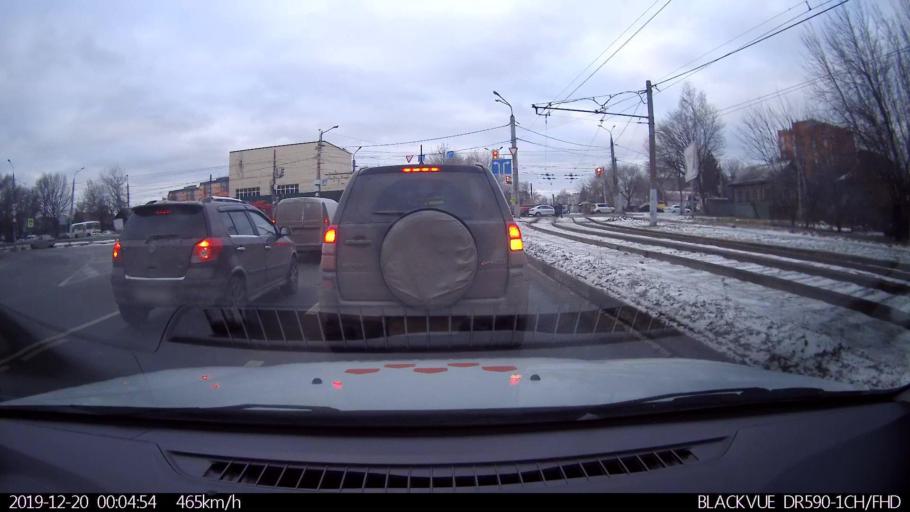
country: RU
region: Jaroslavl
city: Konstantinovskiy
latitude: 57.9837
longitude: 39.7136
